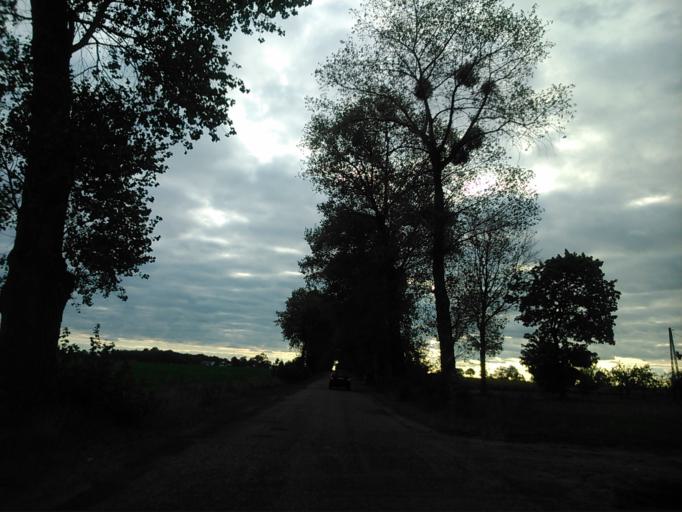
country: PL
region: Kujawsko-Pomorskie
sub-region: Powiat golubsko-dobrzynski
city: Kowalewo Pomorskie
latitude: 53.1251
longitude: 18.9219
